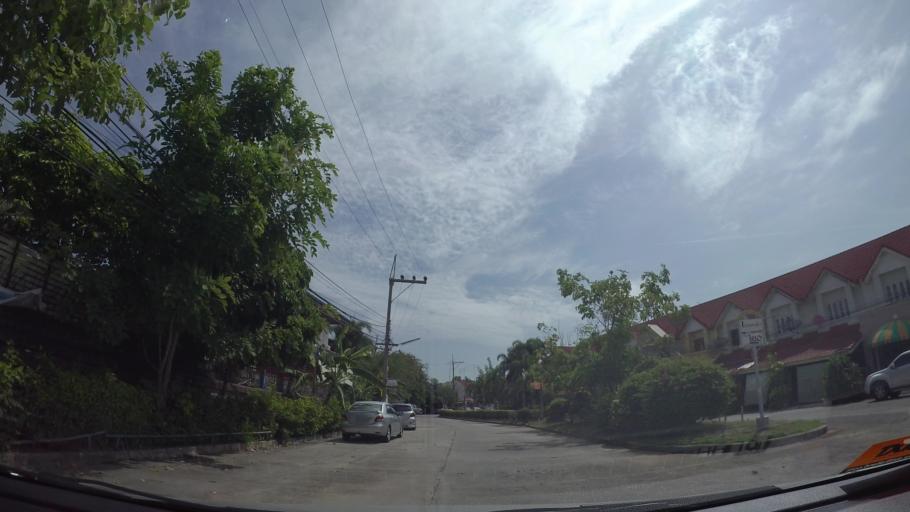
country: TH
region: Chon Buri
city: Chon Buri
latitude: 13.3219
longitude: 100.9471
